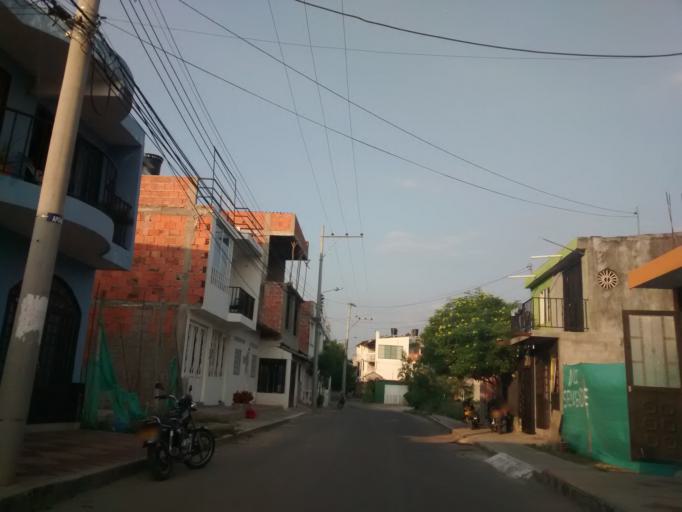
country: CO
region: Cundinamarca
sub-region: Girardot
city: Girardot City
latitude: 4.3165
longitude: -74.7847
